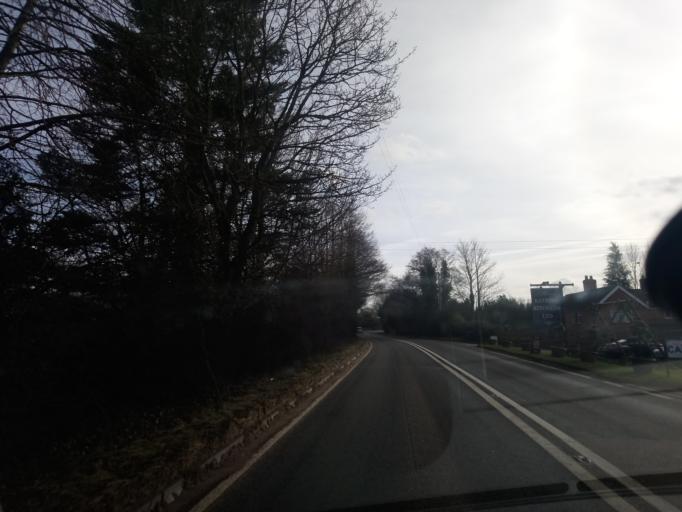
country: GB
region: England
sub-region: Shropshire
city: Prees
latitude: 52.8806
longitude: -2.6554
